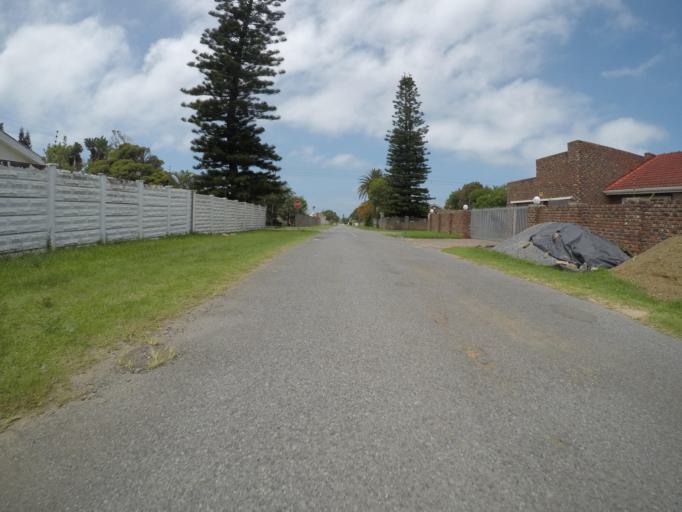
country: ZA
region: Eastern Cape
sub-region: Buffalo City Metropolitan Municipality
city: East London
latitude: -32.9457
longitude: 28.0072
